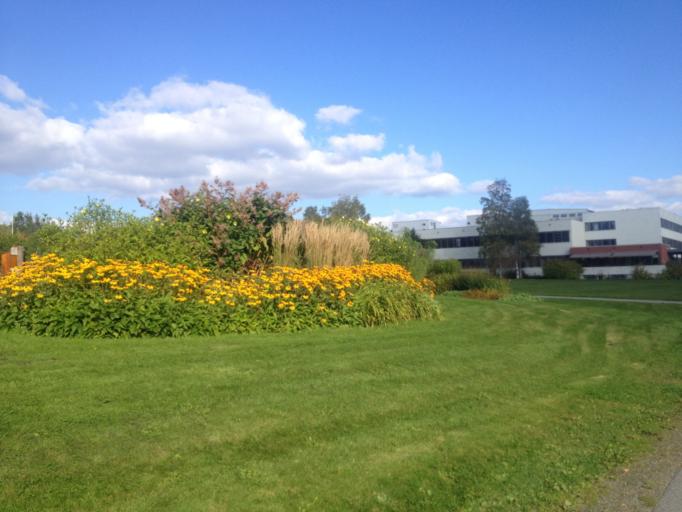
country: NO
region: Akershus
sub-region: As
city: As
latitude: 59.6650
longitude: 10.7741
